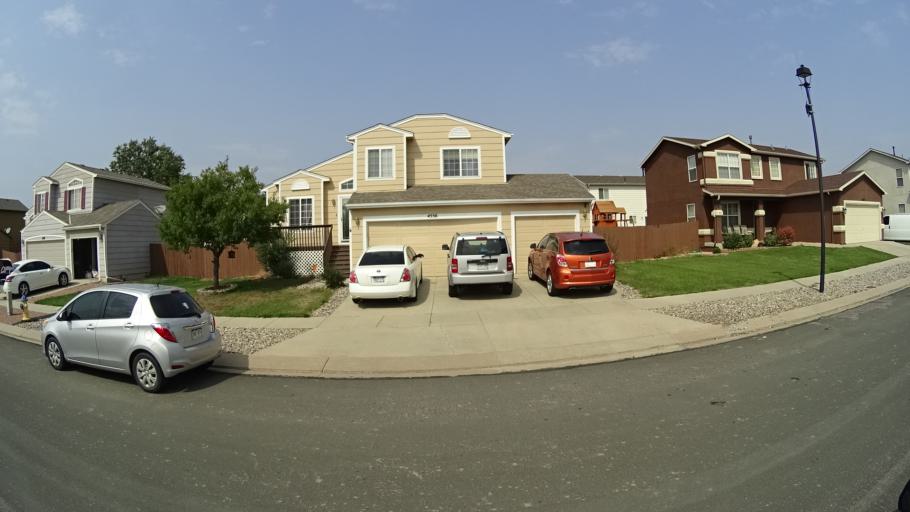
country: US
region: Colorado
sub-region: El Paso County
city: Cimarron Hills
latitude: 38.8269
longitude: -104.7422
